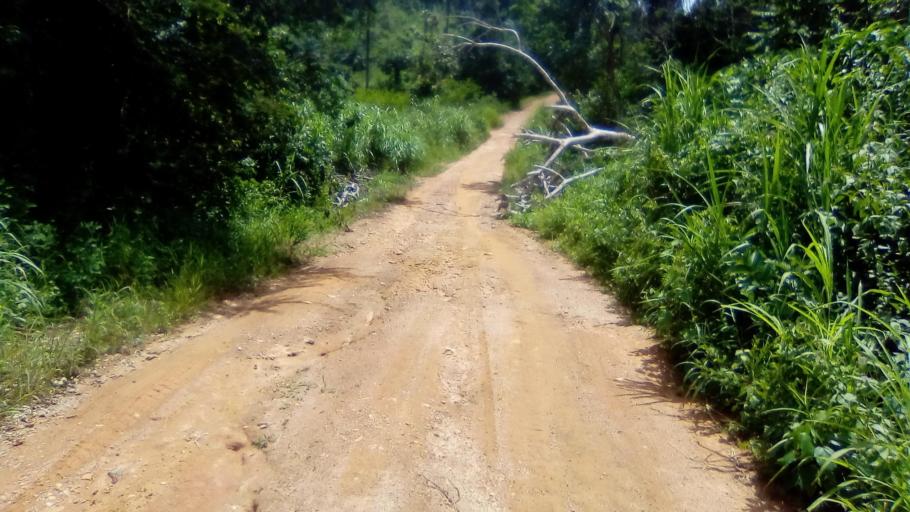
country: SL
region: Eastern Province
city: Simbakoro
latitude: 8.5415
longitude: -10.9390
